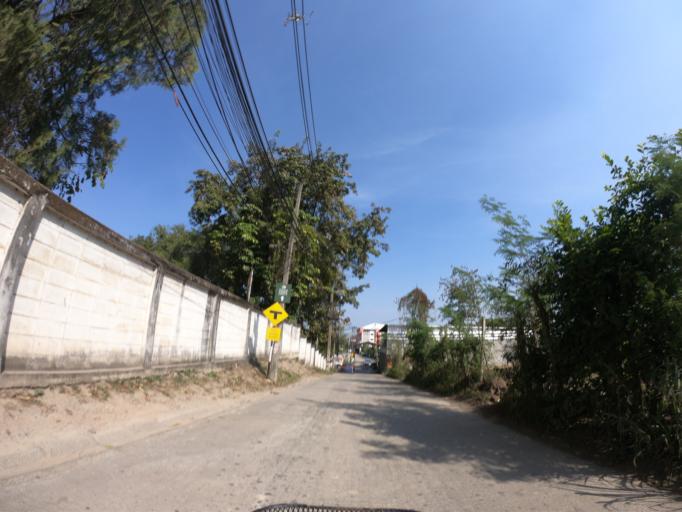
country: TH
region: Chiang Mai
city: Chiang Mai
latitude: 18.8236
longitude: 98.9848
